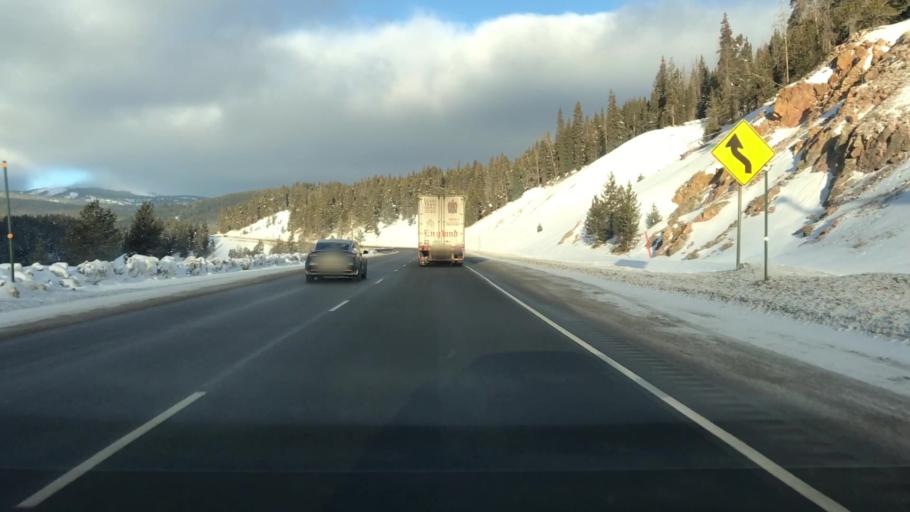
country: US
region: Colorado
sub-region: Summit County
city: Frisco
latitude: 39.5028
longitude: -106.1705
